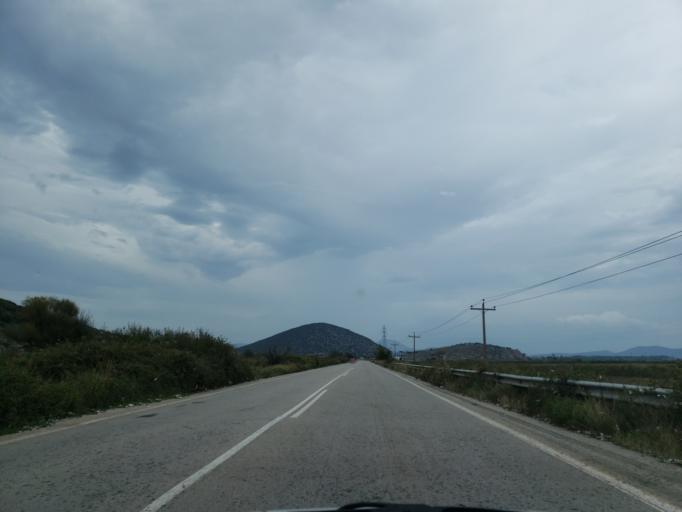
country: GR
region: Central Greece
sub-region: Nomos Voiotias
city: Orchomenos
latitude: 38.4803
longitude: 23.0894
